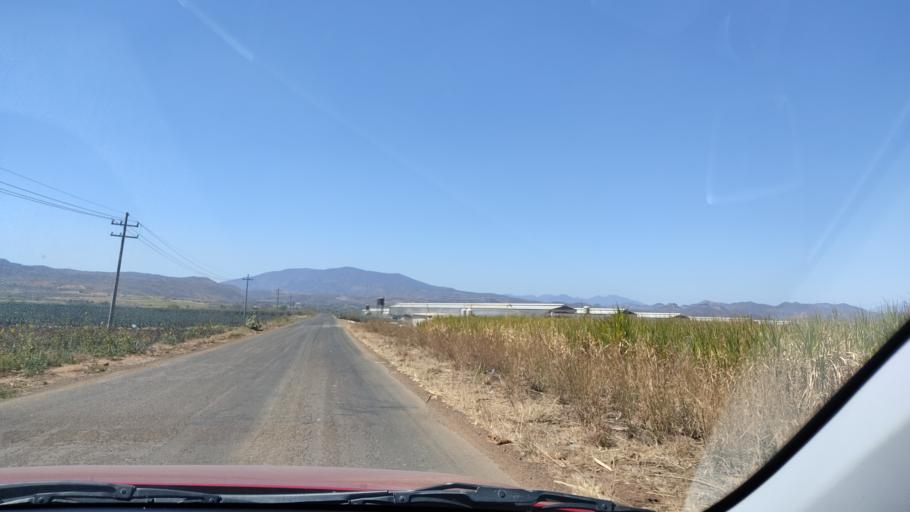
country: MX
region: Nayarit
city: Santa Maria del Oro
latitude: 21.4365
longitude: -104.6205
